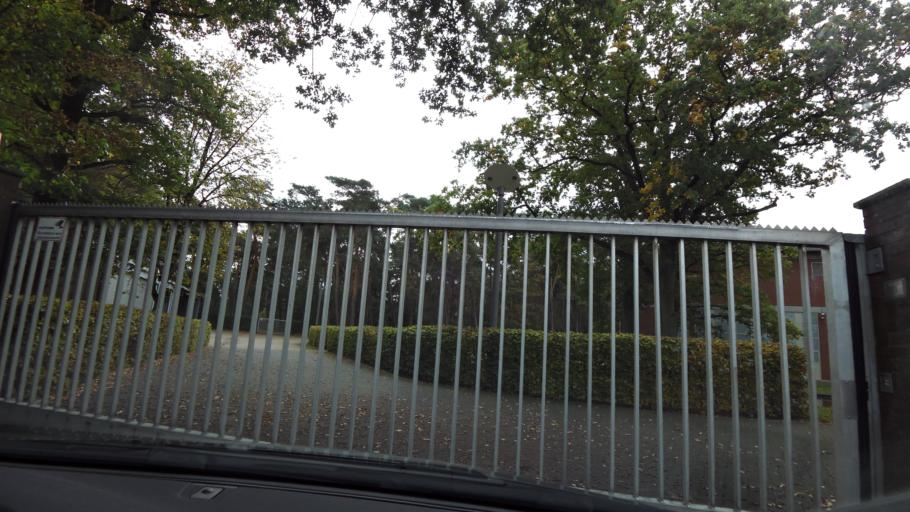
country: DE
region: North Rhine-Westphalia
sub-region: Regierungsbezirk Koln
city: Gangelt
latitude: 50.9801
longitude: 6.0452
